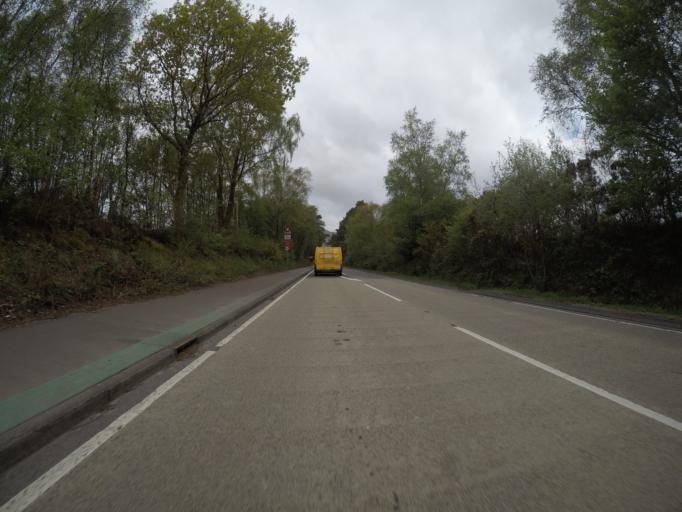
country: GB
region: Scotland
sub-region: Highland
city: Fort William
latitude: 56.7162
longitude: -5.2302
